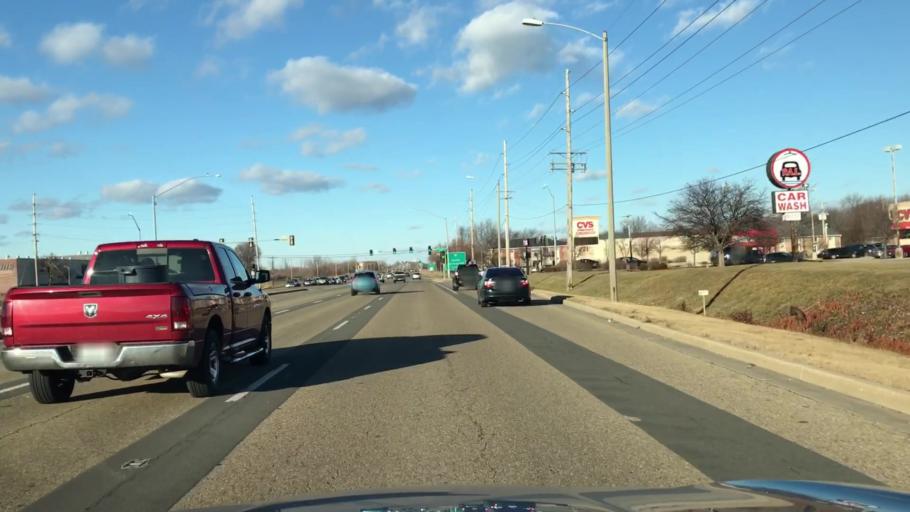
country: US
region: Illinois
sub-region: McLean County
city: Normal
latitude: 40.5162
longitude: -88.9525
